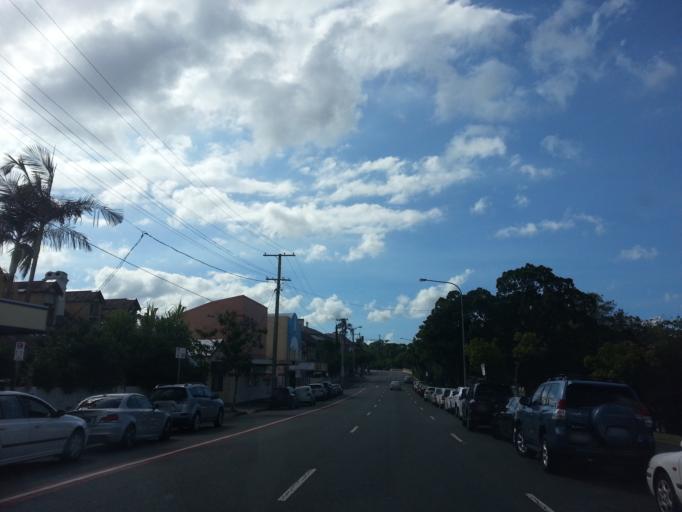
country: AU
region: Queensland
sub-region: Brisbane
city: Spring Hill
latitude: -27.4622
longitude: 153.0145
